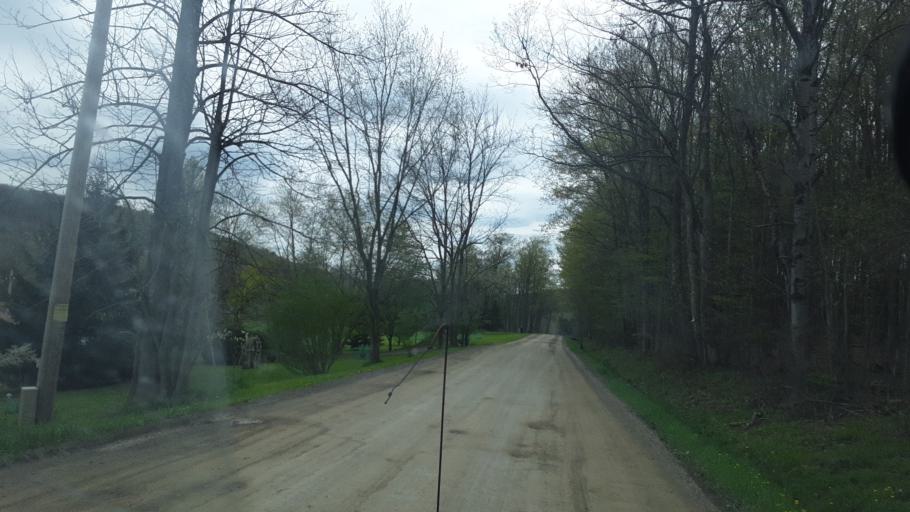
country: US
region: New York
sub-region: Steuben County
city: Addison
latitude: 42.1029
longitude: -77.3393
